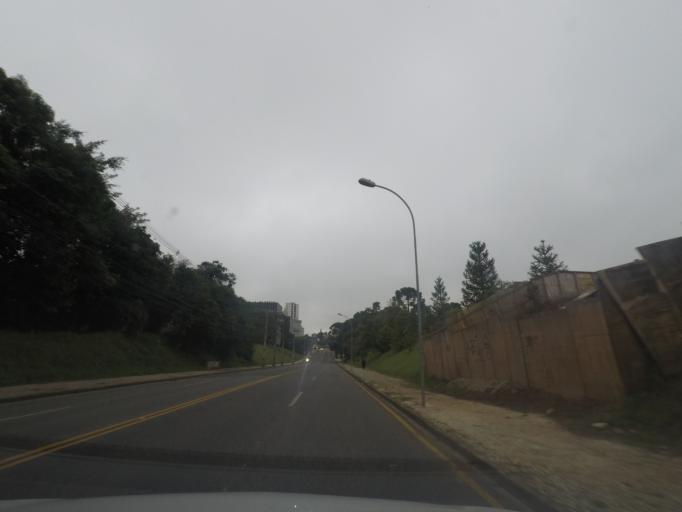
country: BR
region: Parana
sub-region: Curitiba
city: Curitiba
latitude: -25.4121
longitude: -49.2689
